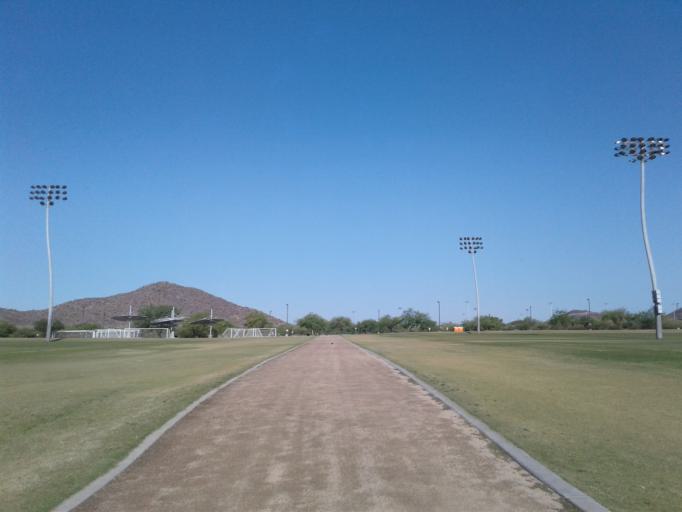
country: US
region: Arizona
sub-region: Maricopa County
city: Cave Creek
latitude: 33.6809
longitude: -112.0224
